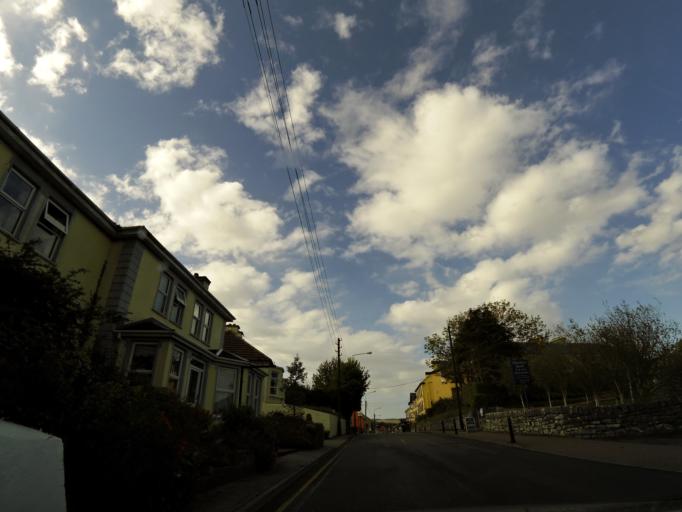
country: IE
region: Connaught
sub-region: County Galway
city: Bearna
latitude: 53.0272
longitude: -9.2900
